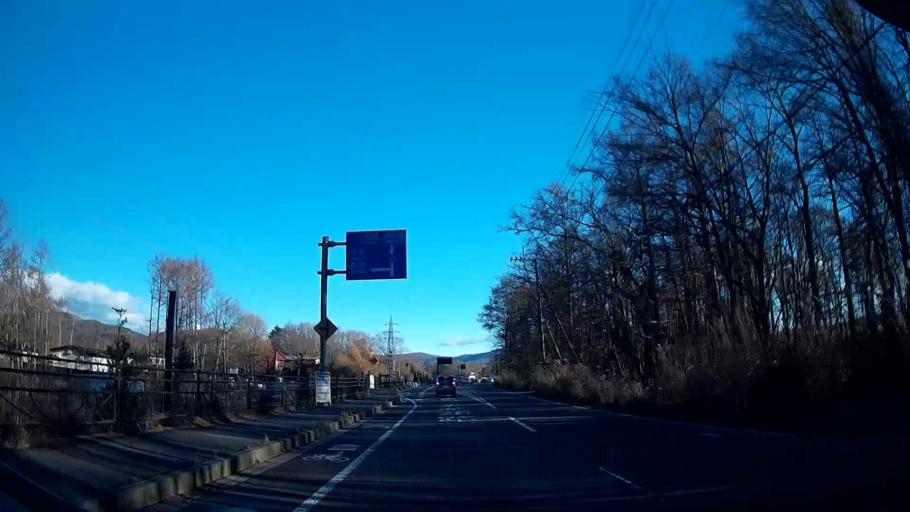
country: JP
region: Yamanashi
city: Fujikawaguchiko
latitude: 35.4376
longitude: 138.8379
